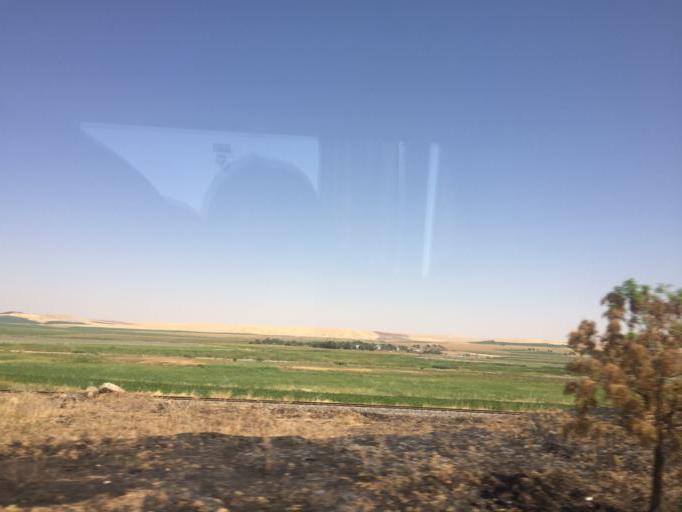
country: TR
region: Diyarbakir
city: Tepe
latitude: 37.8484
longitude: 40.7981
